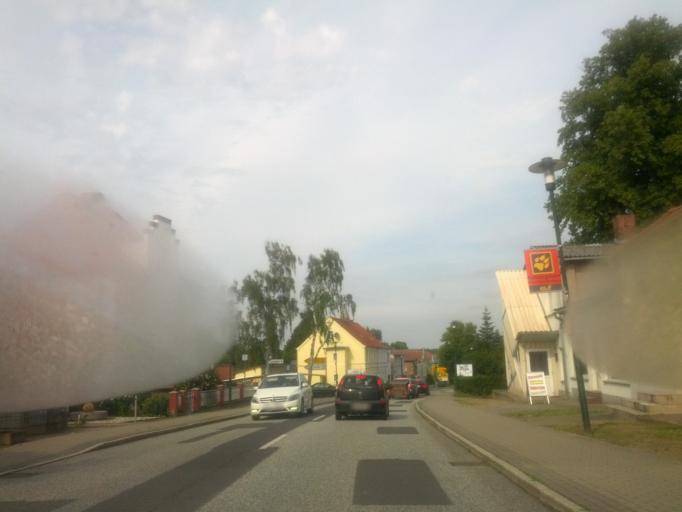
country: DE
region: Mecklenburg-Vorpommern
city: Neubukow
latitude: 54.0280
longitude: 11.6659
